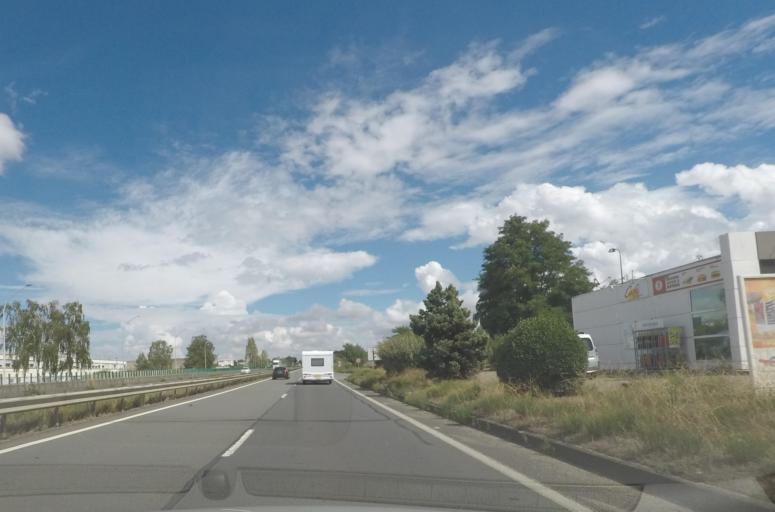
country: FR
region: Pays de la Loire
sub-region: Departement de la Sarthe
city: Arnage
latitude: 47.9484
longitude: 0.1947
